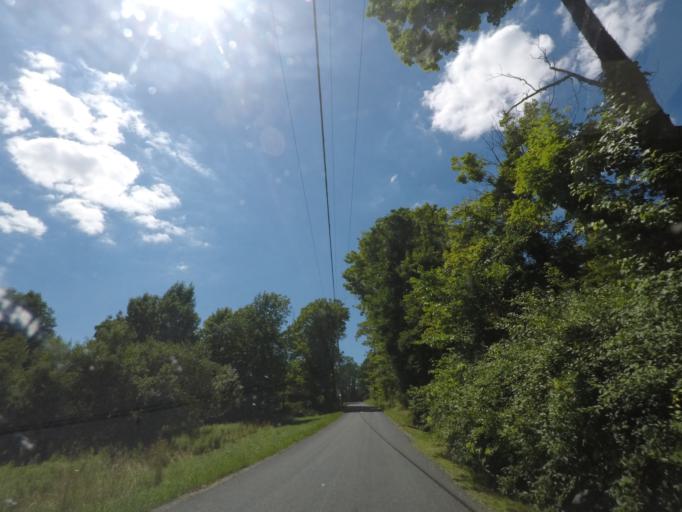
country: US
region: New York
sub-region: Rensselaer County
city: Averill Park
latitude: 42.5757
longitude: -73.5250
